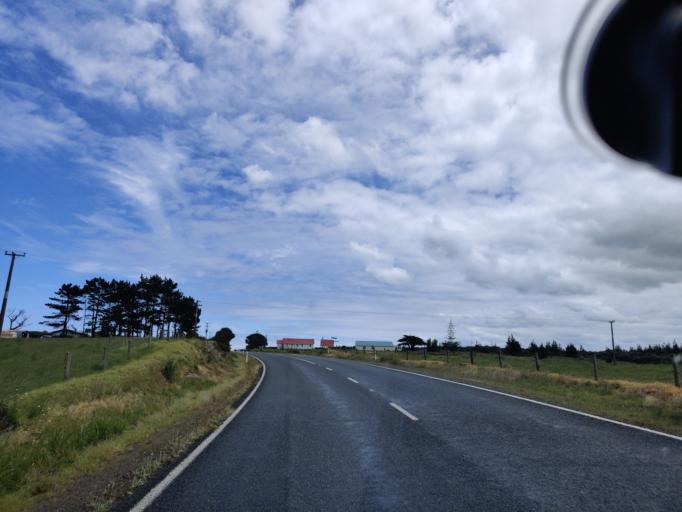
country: NZ
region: Northland
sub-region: Far North District
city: Kaitaia
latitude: -34.6738
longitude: 172.9984
